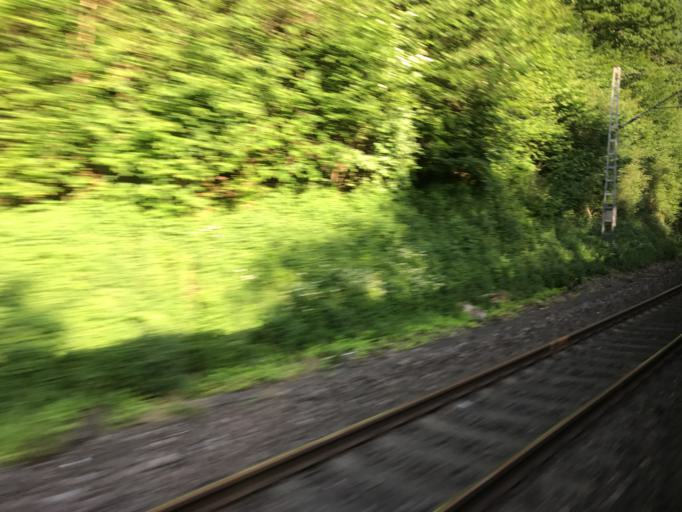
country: DE
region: Saarland
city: Namborn
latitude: 49.5388
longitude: 7.1433
